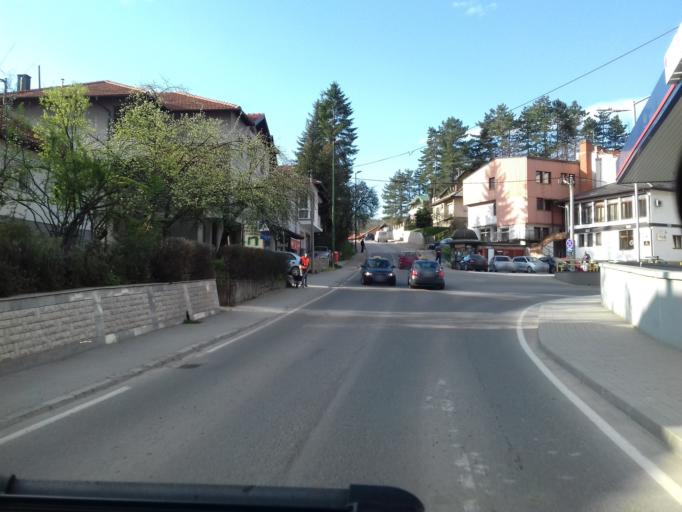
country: BA
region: Federation of Bosnia and Herzegovina
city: Tesanj
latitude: 44.6066
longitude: 17.9867
